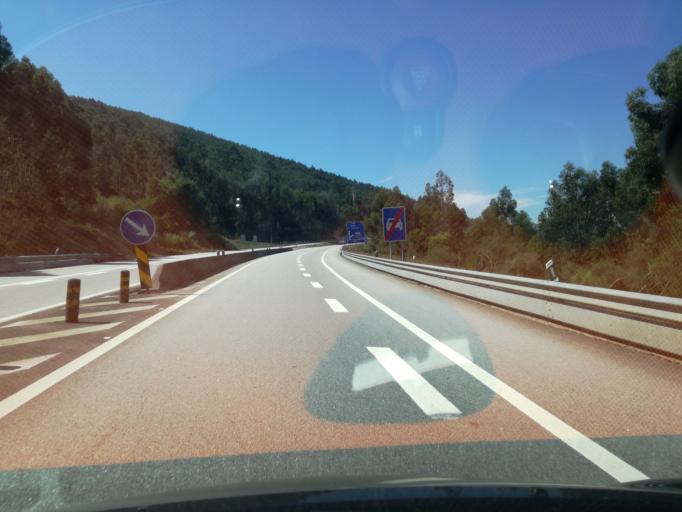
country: PT
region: Viana do Castelo
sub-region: Vila Nova de Cerveira
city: Vila Nova de Cerveira
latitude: 41.8878
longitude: -8.7759
